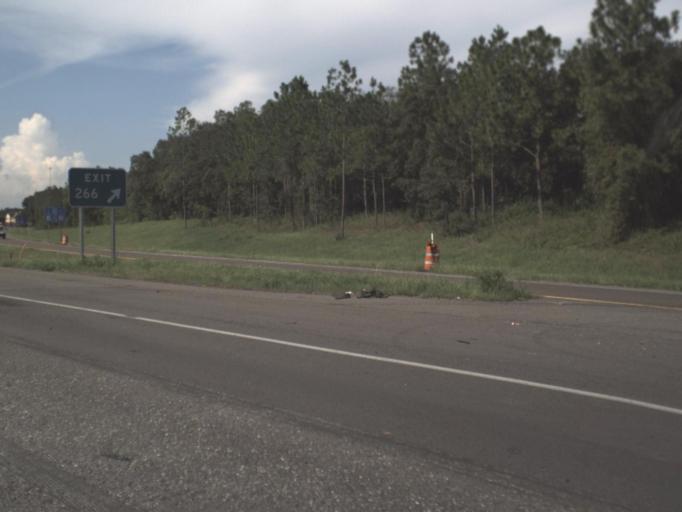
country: US
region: Florida
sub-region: Hillsborough County
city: Temple Terrace
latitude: 28.0750
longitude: -82.3540
